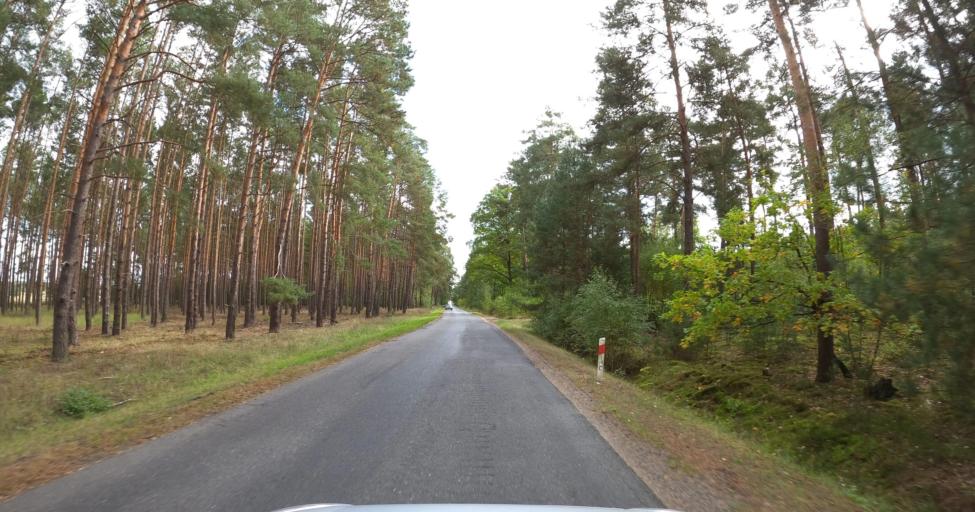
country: PL
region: Lubusz
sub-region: Zielona Gora
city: Zielona Gora
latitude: 51.9772
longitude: 15.5956
